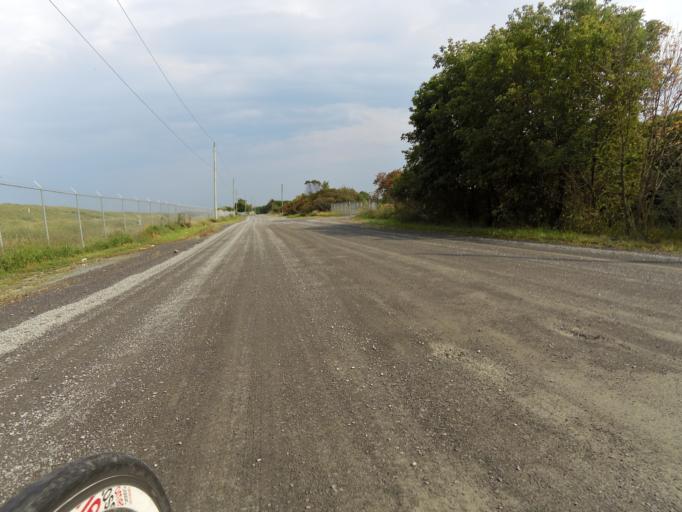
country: CA
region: Ontario
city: Bells Corners
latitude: 45.2315
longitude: -75.7646
